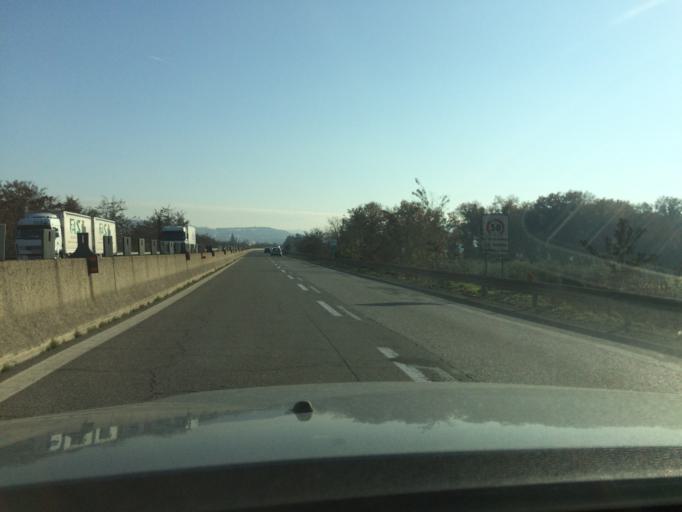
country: IT
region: Umbria
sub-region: Provincia di Perugia
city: Ponterio-Pian di Porto
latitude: 42.8165
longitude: 12.4024
